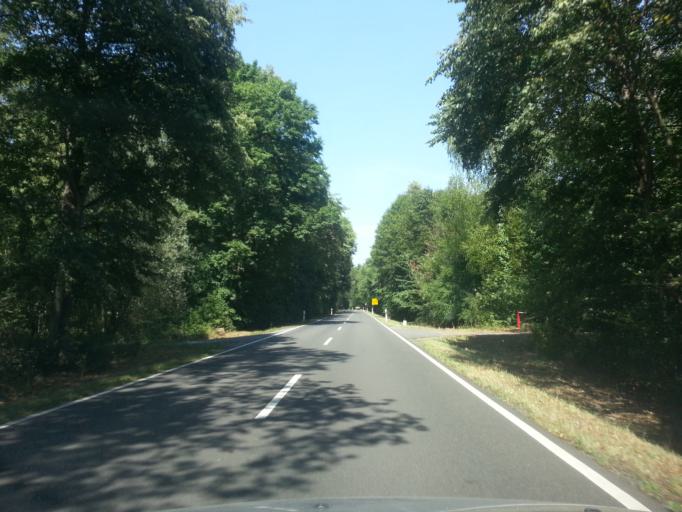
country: DE
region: Hesse
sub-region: Regierungsbezirk Darmstadt
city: Gross-Rohrheim
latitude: 49.7020
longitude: 8.5150
